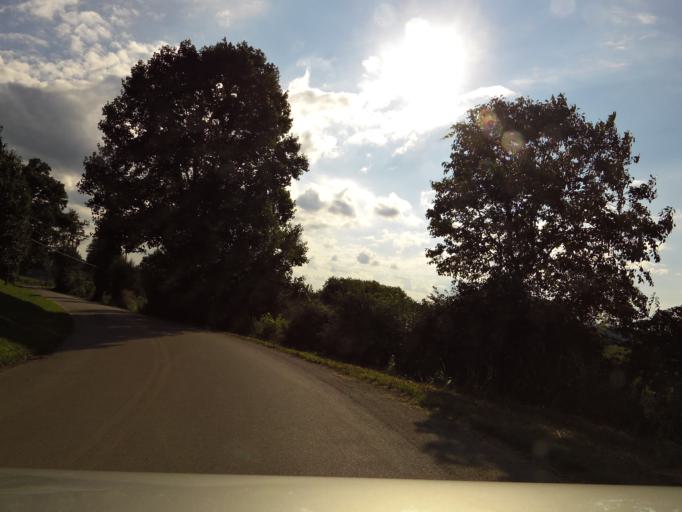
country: US
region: Tennessee
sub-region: Loudon County
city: Greenback
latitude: 35.6612
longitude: -84.0938
